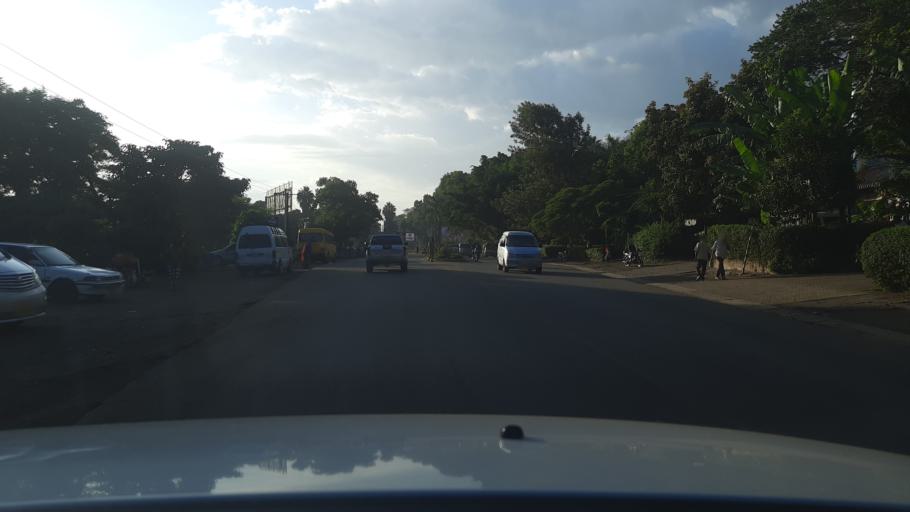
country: TZ
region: Arusha
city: Arusha
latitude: -3.3782
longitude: 36.7044
